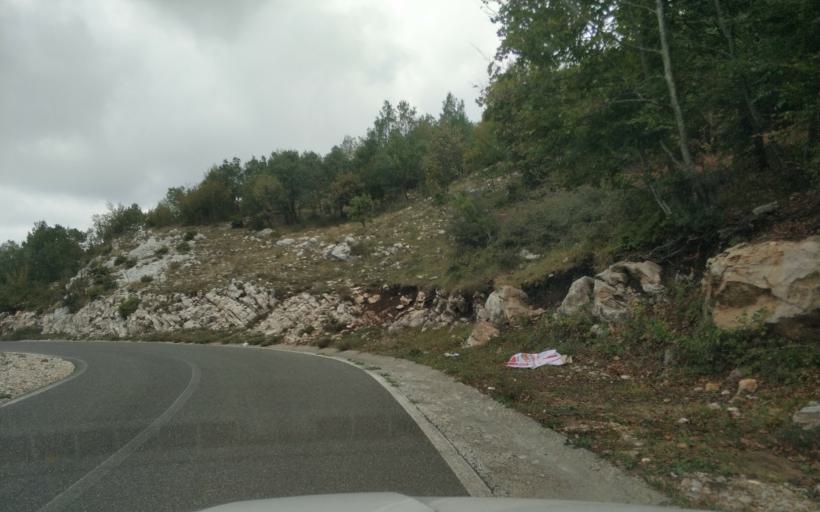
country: AL
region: Durres
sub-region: Rrethi i Krujes
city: Kruje
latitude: 41.5201
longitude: 19.8064
